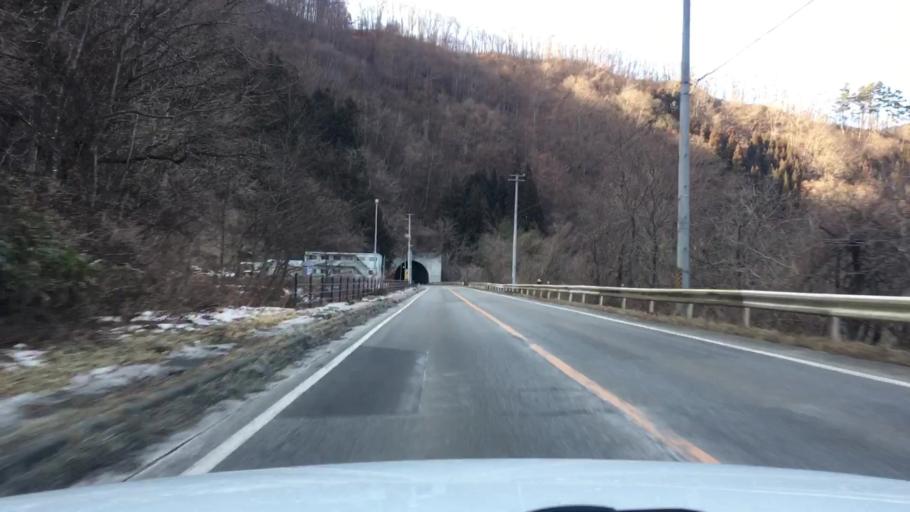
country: JP
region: Iwate
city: Tono
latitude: 39.6203
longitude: 141.6212
